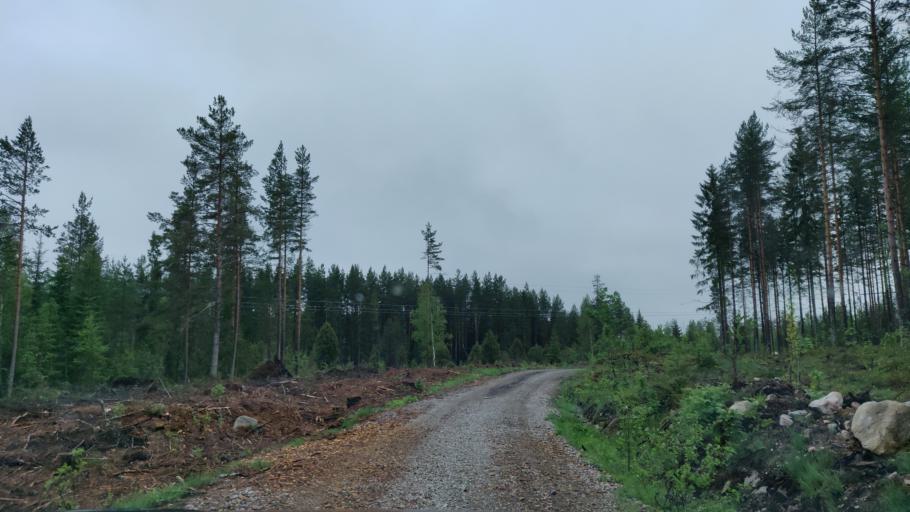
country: SE
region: Dalarna
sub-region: Avesta Kommun
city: Horndal
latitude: 60.3074
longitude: 16.4025
